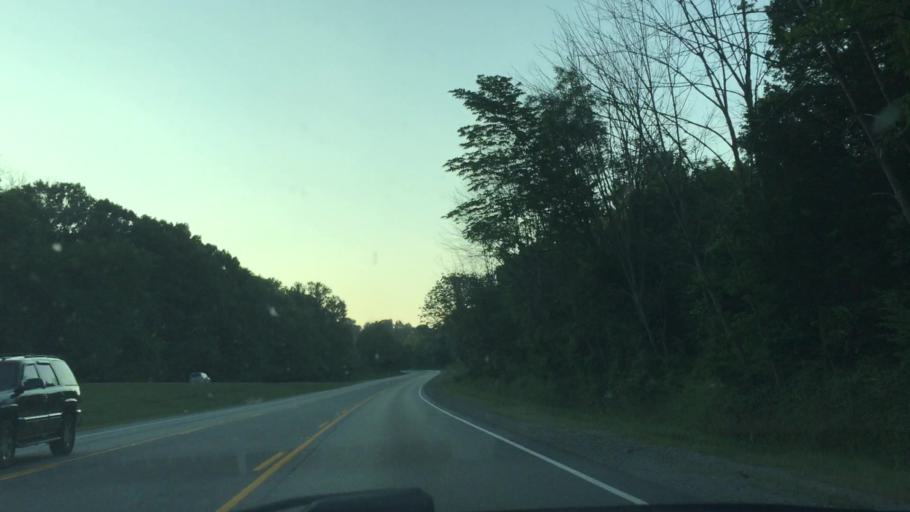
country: US
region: Kentucky
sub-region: Carroll County
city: Carrollton
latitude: 38.6710
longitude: -85.1469
